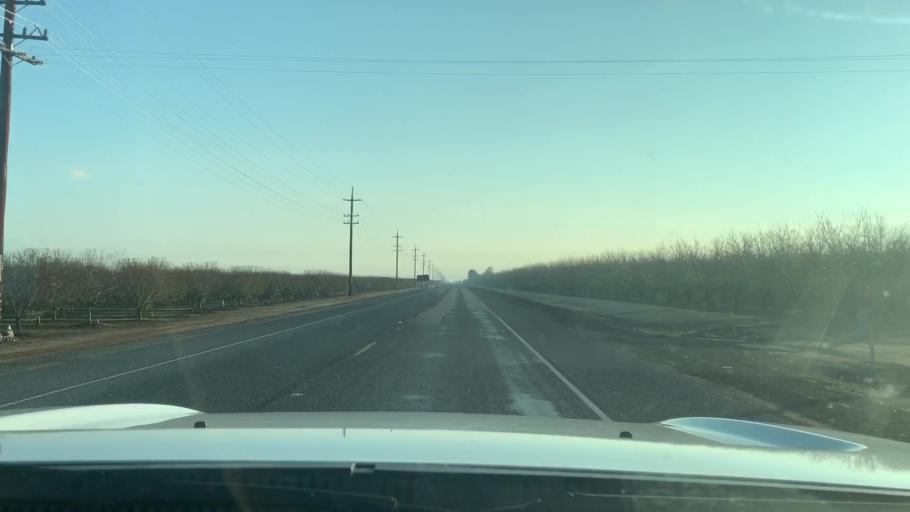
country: US
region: California
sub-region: Kern County
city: Wasco
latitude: 35.6014
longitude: -119.4338
